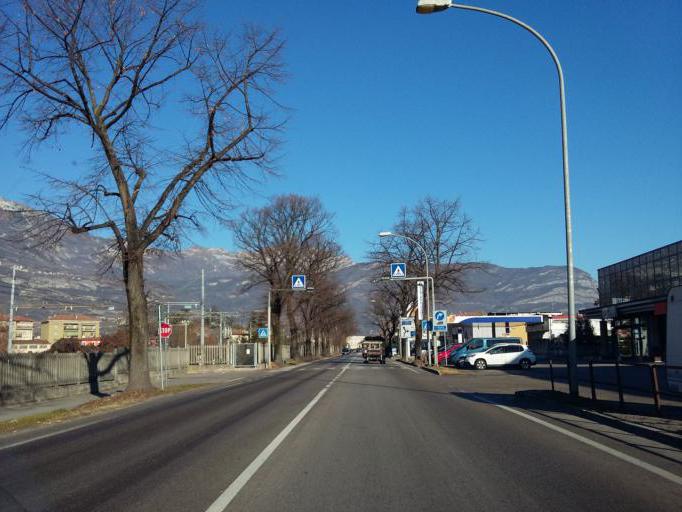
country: IT
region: Trentino-Alto Adige
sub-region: Provincia di Trento
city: Rovereto
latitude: 45.8844
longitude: 11.0327
